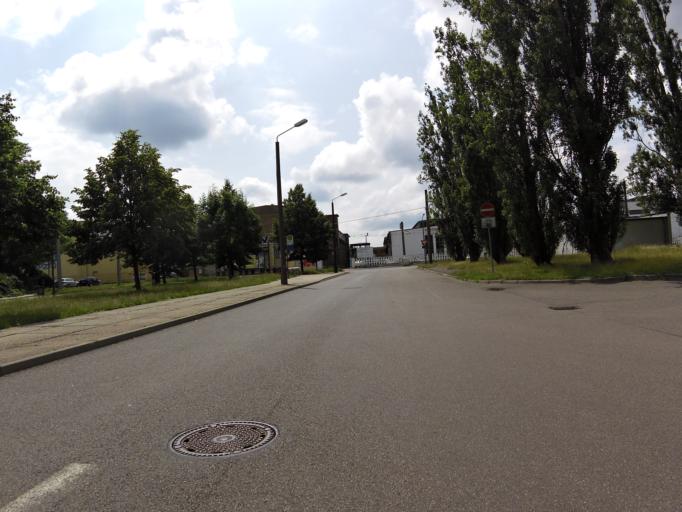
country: DE
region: Saxony
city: Taucha
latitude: 51.3463
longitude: 12.4576
